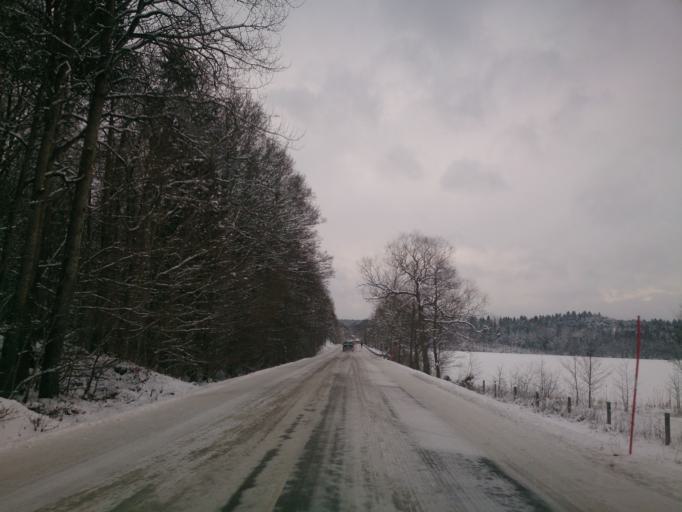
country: SE
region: OEstergoetland
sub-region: Atvidabergs Kommun
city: Atvidaberg
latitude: 58.3433
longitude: 16.0274
